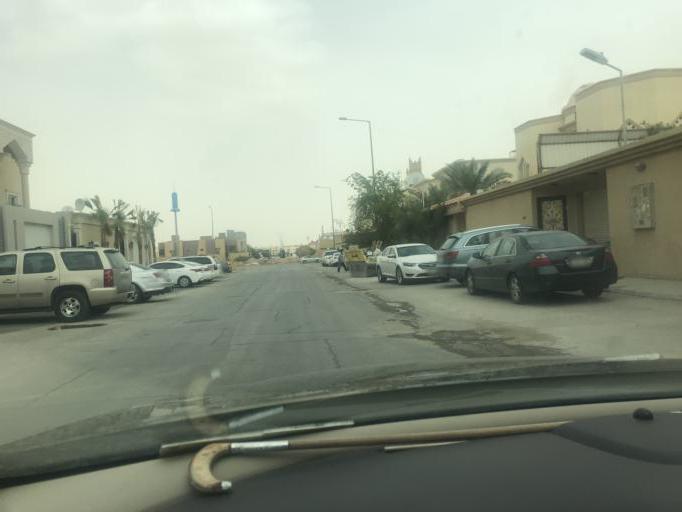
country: SA
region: Ar Riyad
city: Riyadh
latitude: 24.7361
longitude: 46.7874
